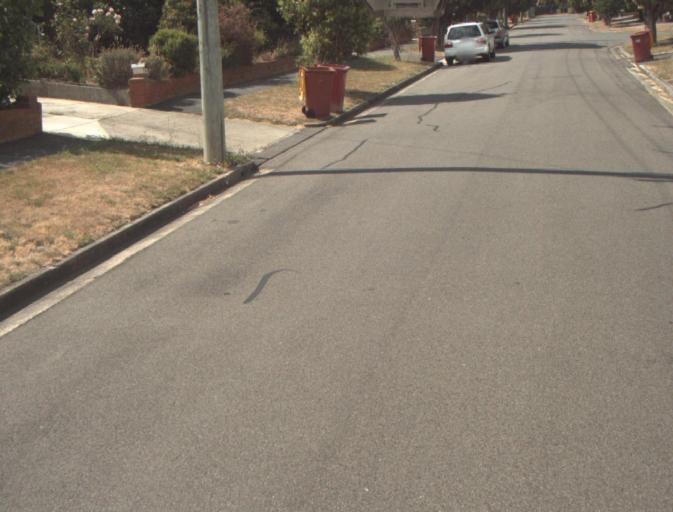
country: AU
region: Tasmania
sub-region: Launceston
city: Summerhill
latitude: -41.4669
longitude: 147.1439
